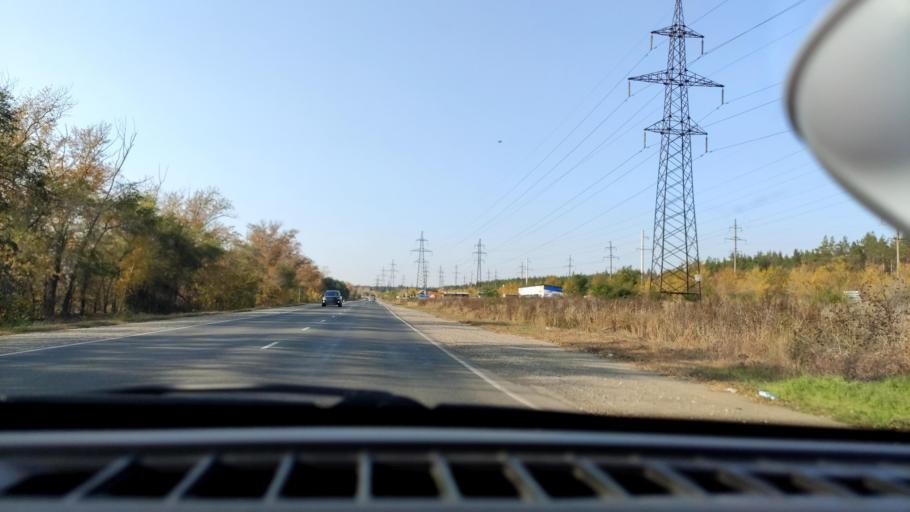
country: RU
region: Samara
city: Samara
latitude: 53.1165
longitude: 50.2222
